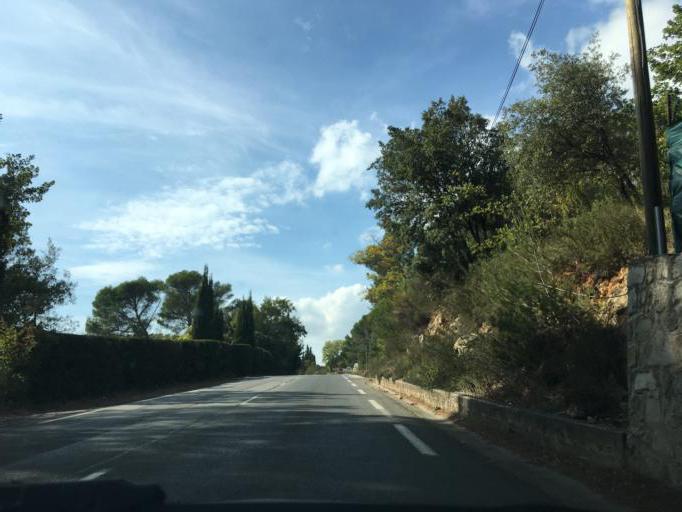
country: FR
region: Provence-Alpes-Cote d'Azur
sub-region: Departement du Var
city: Flayosc
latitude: 43.5414
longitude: 6.3718
